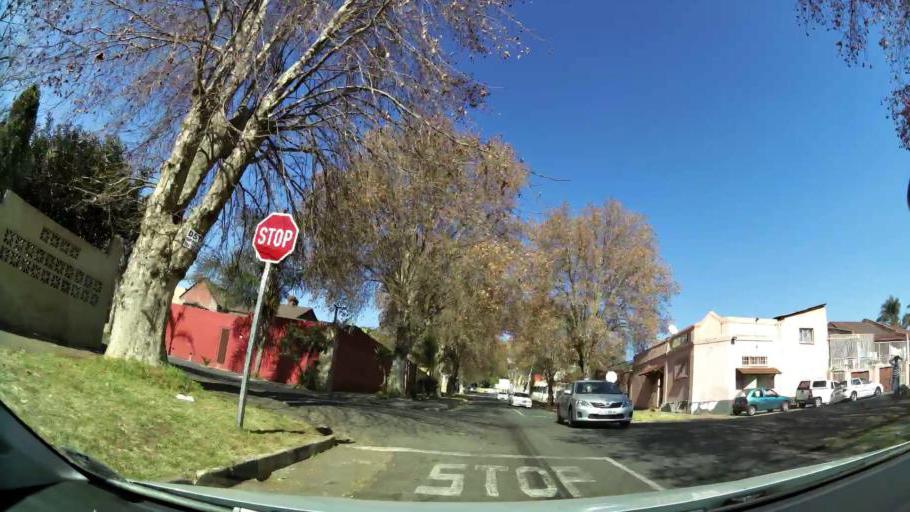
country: ZA
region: Gauteng
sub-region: City of Johannesburg Metropolitan Municipality
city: Johannesburg
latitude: -26.1953
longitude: 28.0696
